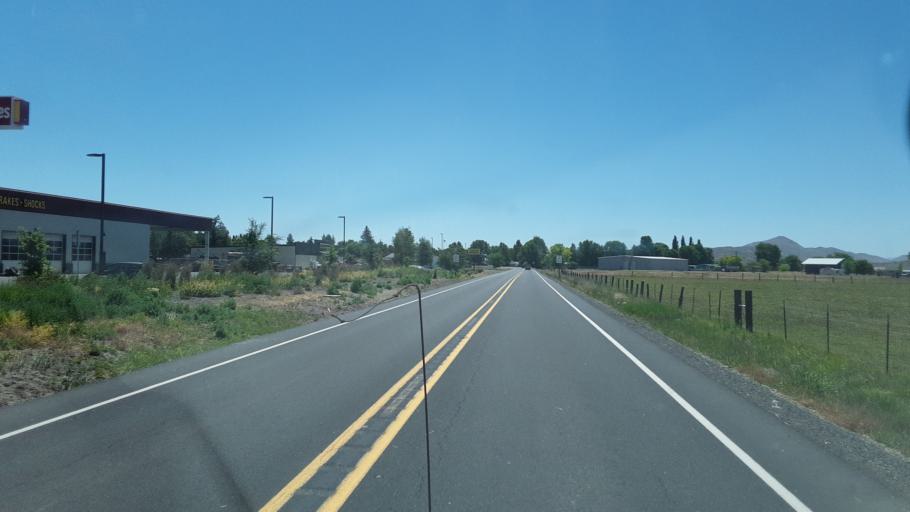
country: US
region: California
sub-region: Siskiyou County
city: Tulelake
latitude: 42.0273
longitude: -121.6107
